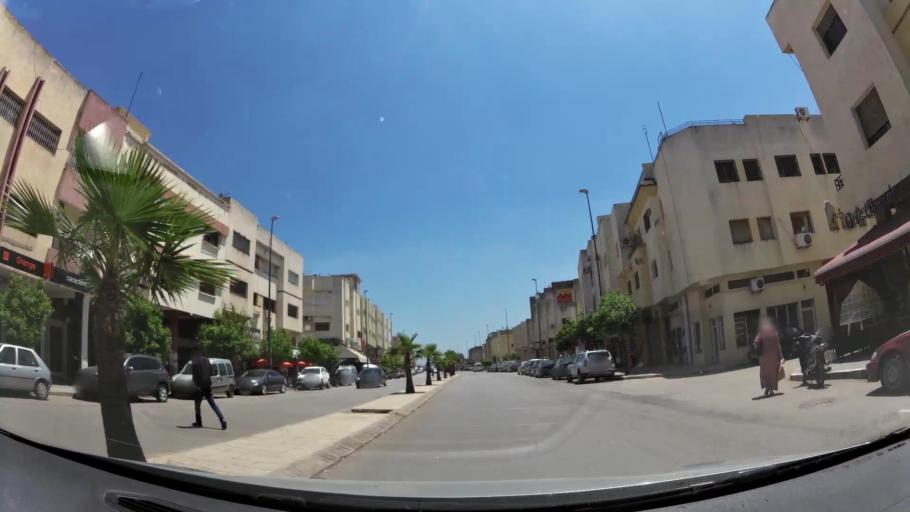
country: MA
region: Fes-Boulemane
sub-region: Fes
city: Fes
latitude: 34.0223
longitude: -5.0121
